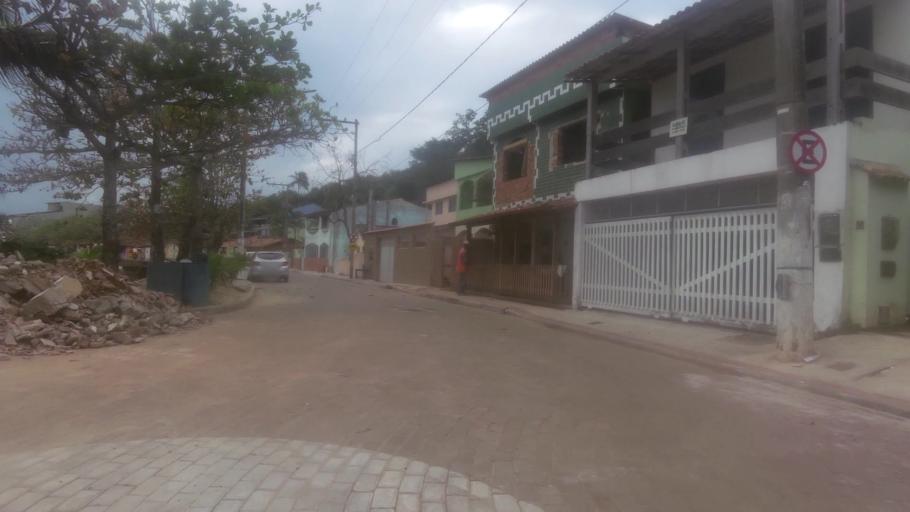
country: BR
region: Espirito Santo
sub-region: Piuma
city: Piuma
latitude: -20.8036
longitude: -40.5868
